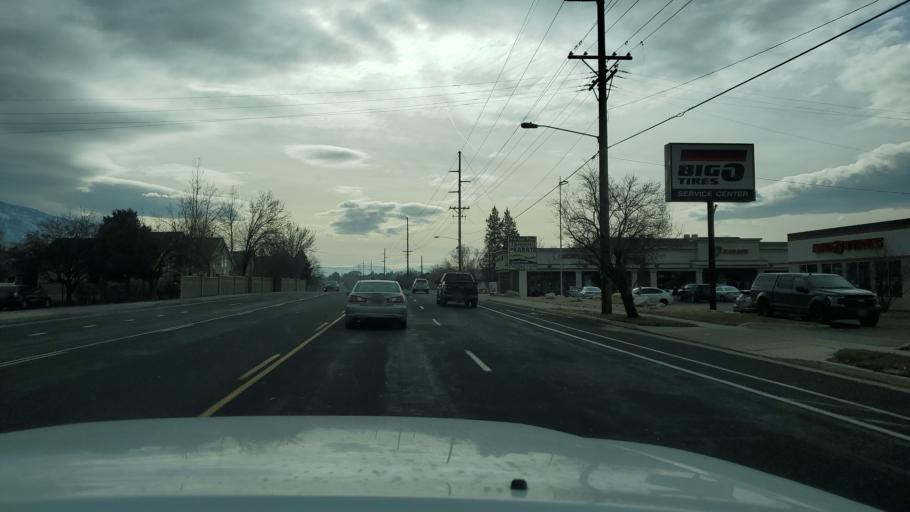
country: US
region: Utah
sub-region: Salt Lake County
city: Millcreek
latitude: 40.6732
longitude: -111.8656
